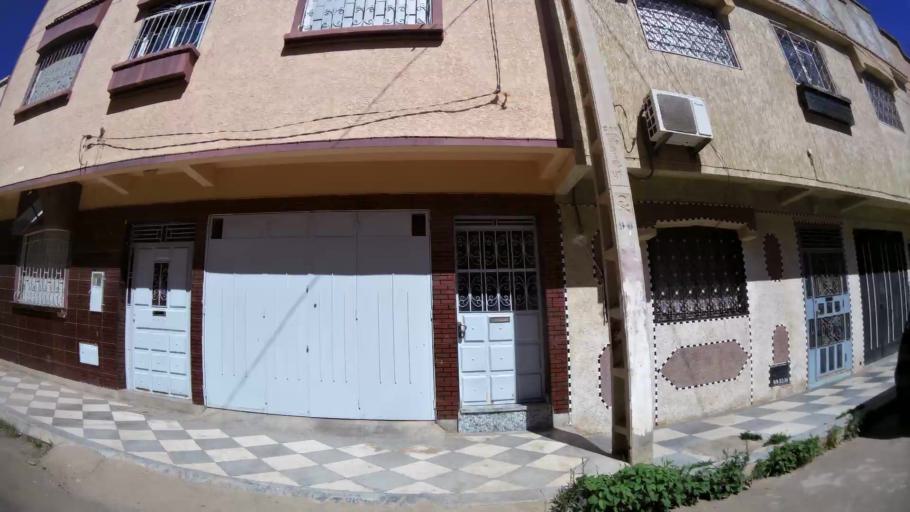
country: MA
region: Oriental
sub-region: Oujda-Angad
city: Oujda
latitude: 34.6608
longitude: -1.9306
